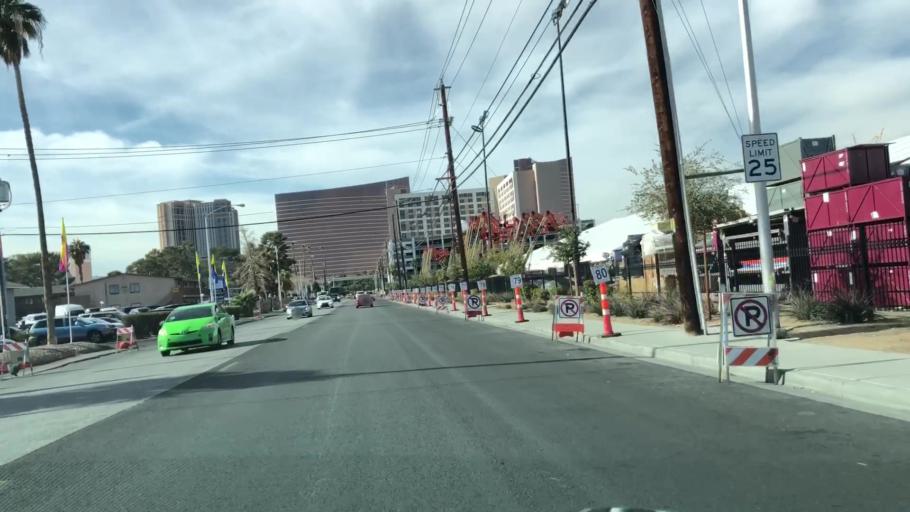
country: US
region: Nevada
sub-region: Clark County
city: Paradise
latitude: 36.1269
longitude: -115.1501
